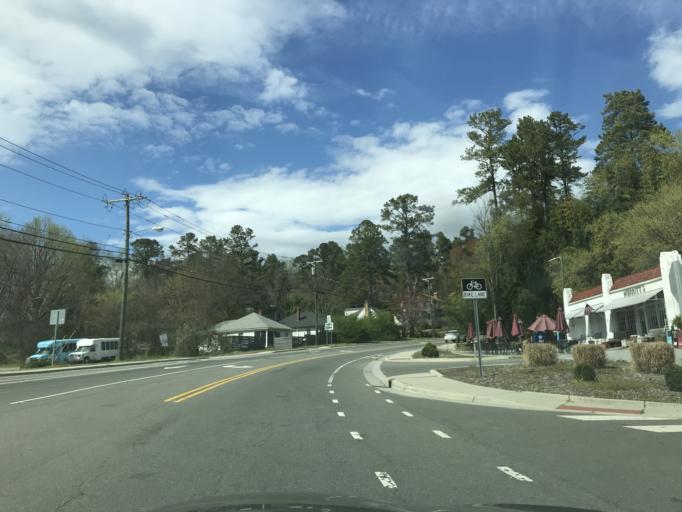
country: US
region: North Carolina
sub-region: Orange County
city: Chapel Hill
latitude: 35.8957
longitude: -79.0585
